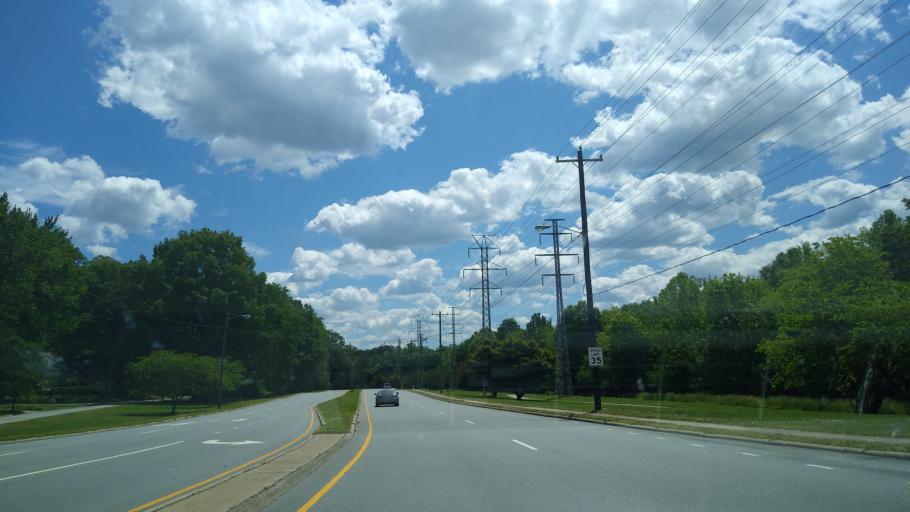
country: US
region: North Carolina
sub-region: Guilford County
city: Greensboro
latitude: 36.0797
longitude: -79.8129
